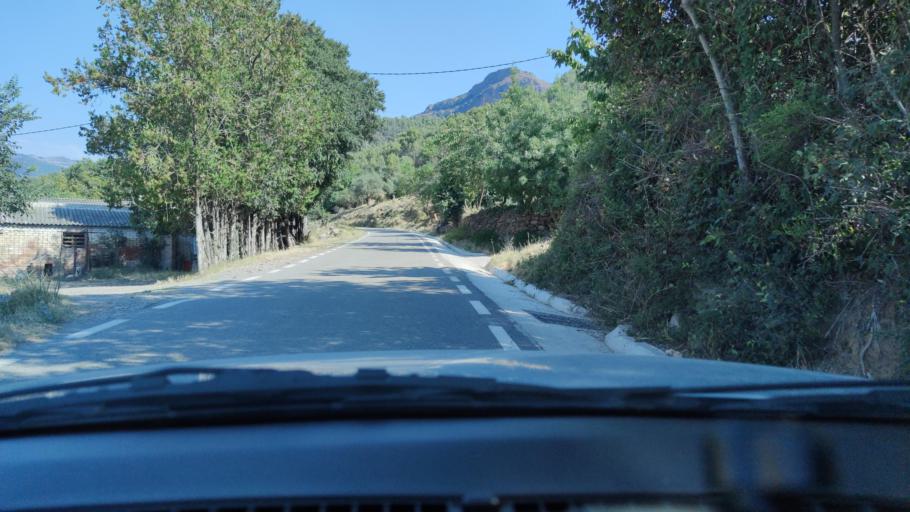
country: ES
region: Catalonia
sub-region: Provincia de Lleida
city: Senterada
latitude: 42.2572
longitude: 0.9627
